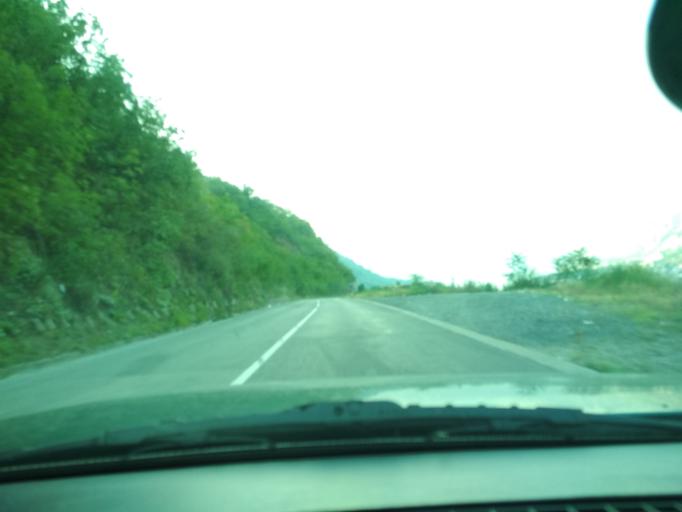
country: ME
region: Kotor
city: Kotor
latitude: 42.4087
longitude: 18.7654
